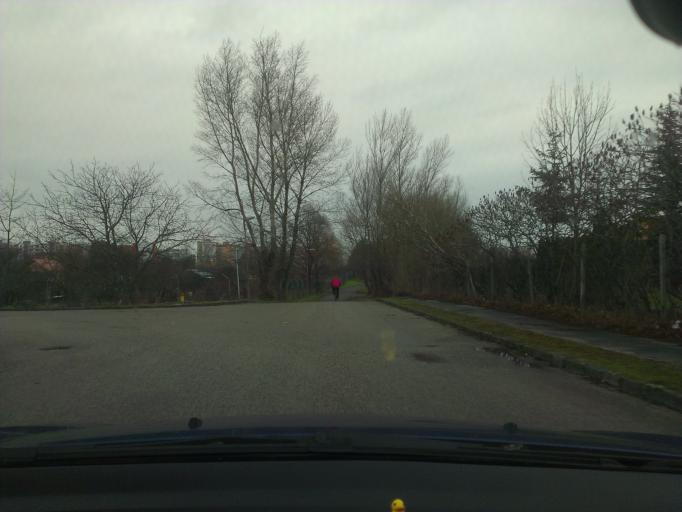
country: SK
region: Trnavsky
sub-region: Okres Trnava
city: Piestany
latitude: 48.5802
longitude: 17.8182
